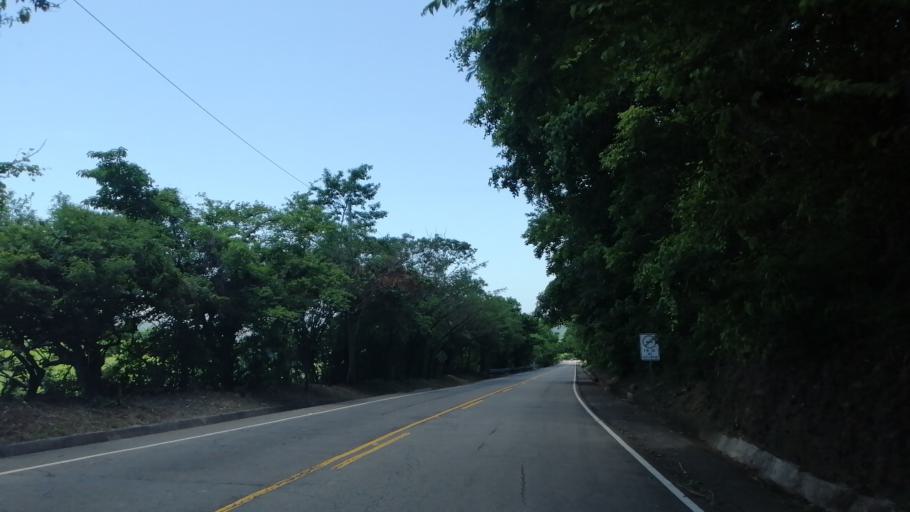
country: SV
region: Chalatenango
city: Nueva Concepcion
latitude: 14.1580
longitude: -89.3099
